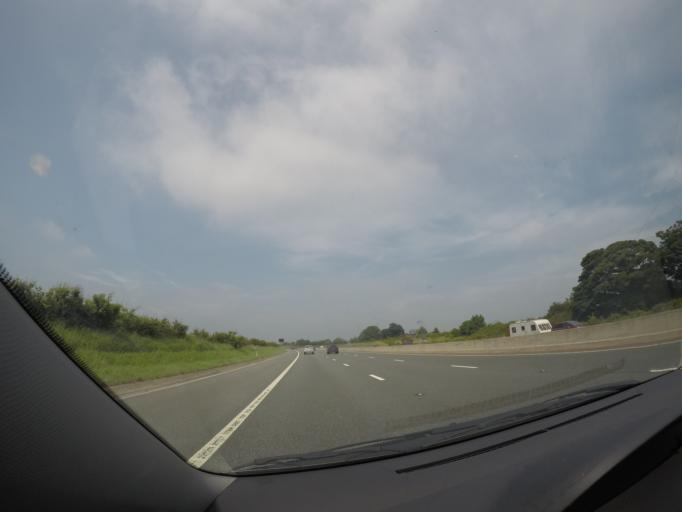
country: GB
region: England
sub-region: North Yorkshire
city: Bedale
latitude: 54.2771
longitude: -1.5312
